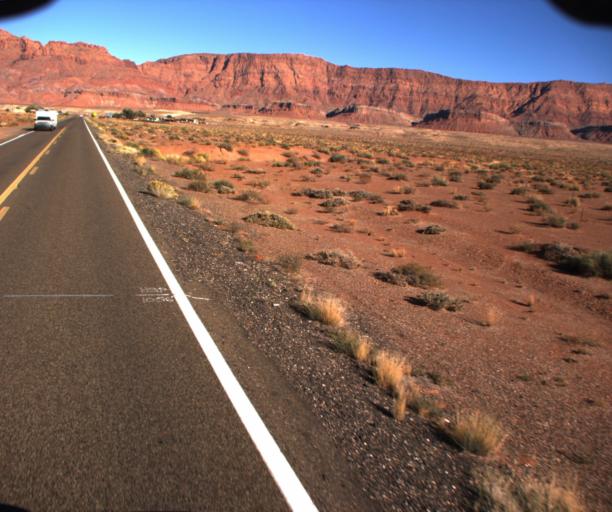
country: US
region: Arizona
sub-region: Coconino County
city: Page
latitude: 36.8144
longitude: -111.6467
